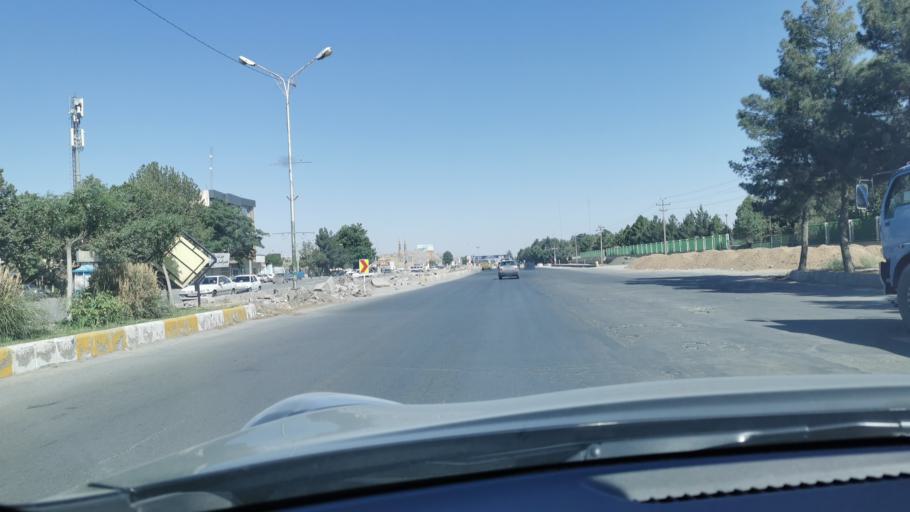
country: IR
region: Razavi Khorasan
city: Chenaran
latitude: 36.6389
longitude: 59.1216
